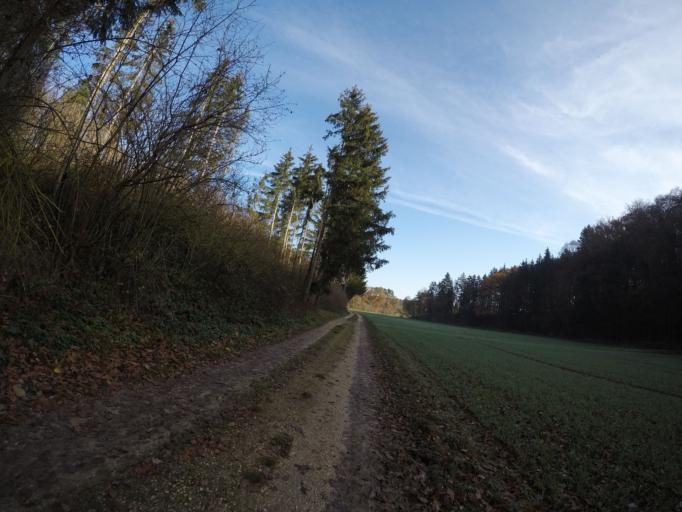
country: DE
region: Baden-Wuerttemberg
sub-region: Tuebingen Region
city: Bernstadt
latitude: 48.5164
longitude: 10.0287
